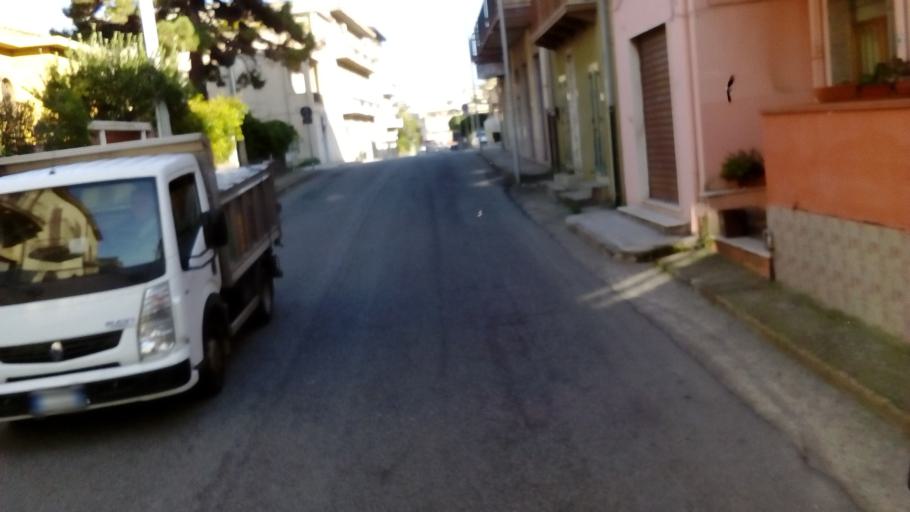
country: IT
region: Calabria
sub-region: Provincia di Reggio Calabria
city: Campo Calabro
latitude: 38.2097
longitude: 15.6362
